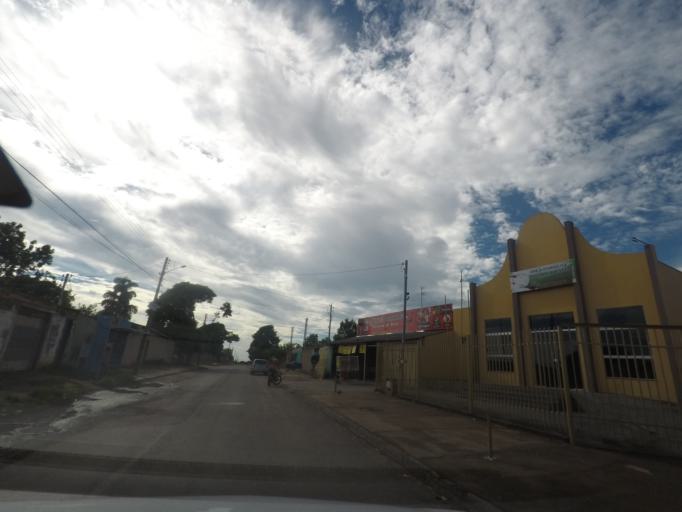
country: BR
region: Goias
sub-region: Aparecida De Goiania
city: Aparecida de Goiania
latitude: -16.8325
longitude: -49.2993
